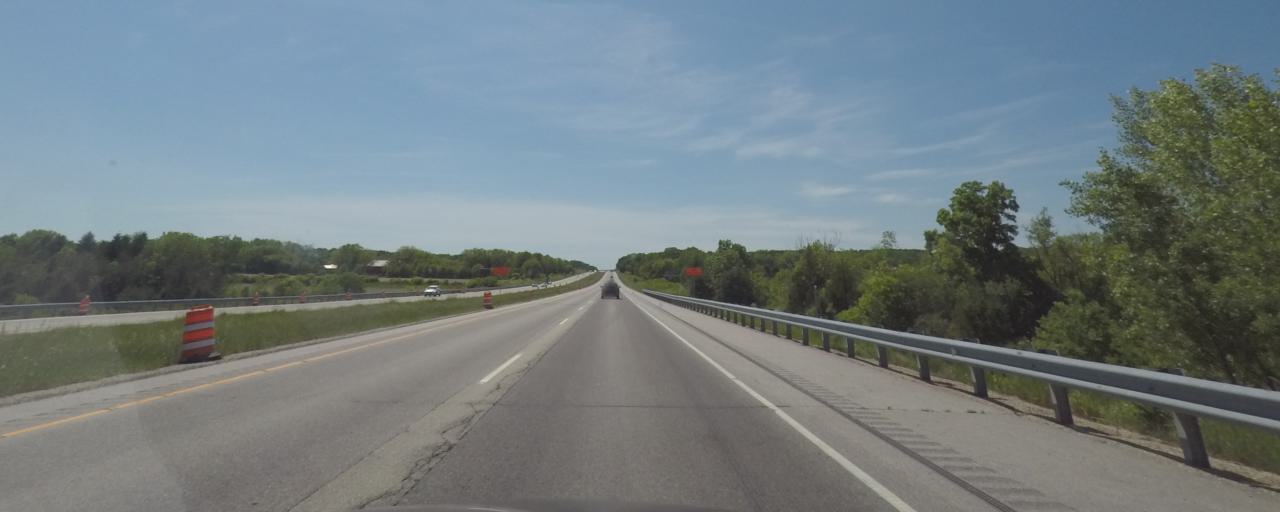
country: US
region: Wisconsin
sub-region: Jefferson County
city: Waterloo
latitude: 43.1111
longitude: -88.9869
